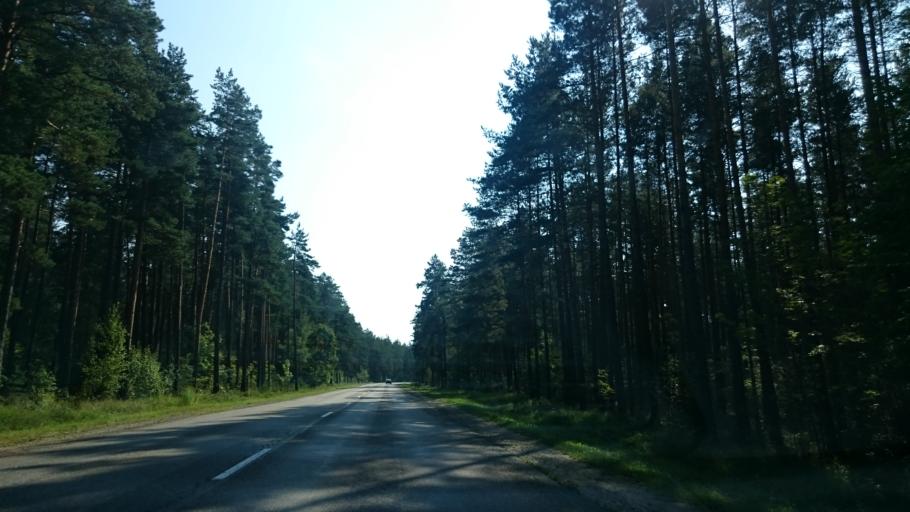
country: LV
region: Stopini
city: Ulbroka
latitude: 56.9565
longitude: 24.3092
